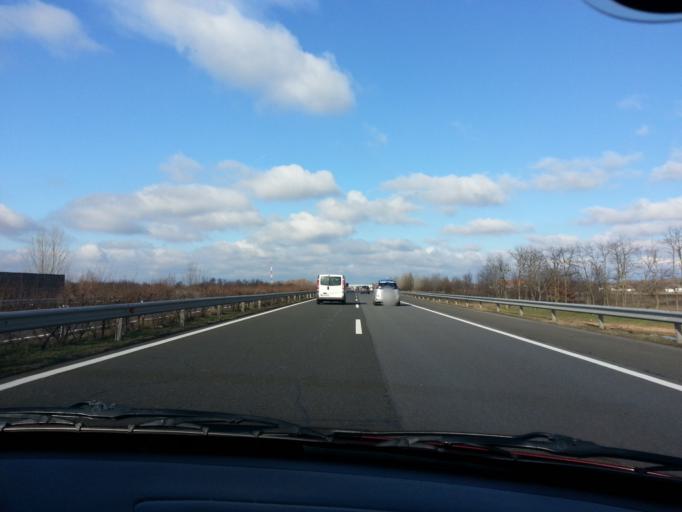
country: HU
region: Csongrad
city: Balastya
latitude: 46.3974
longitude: 19.9790
